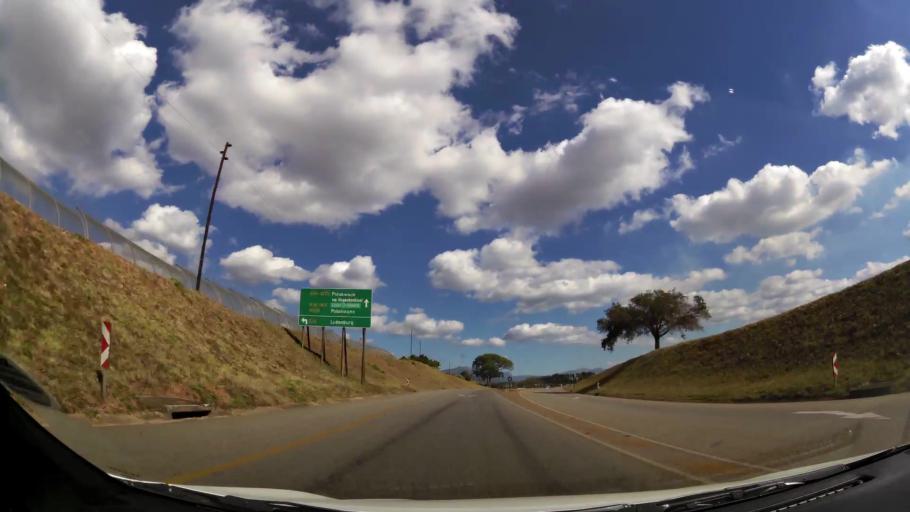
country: ZA
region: Limpopo
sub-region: Mopani District Municipality
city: Tzaneen
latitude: -23.8332
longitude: 30.1388
